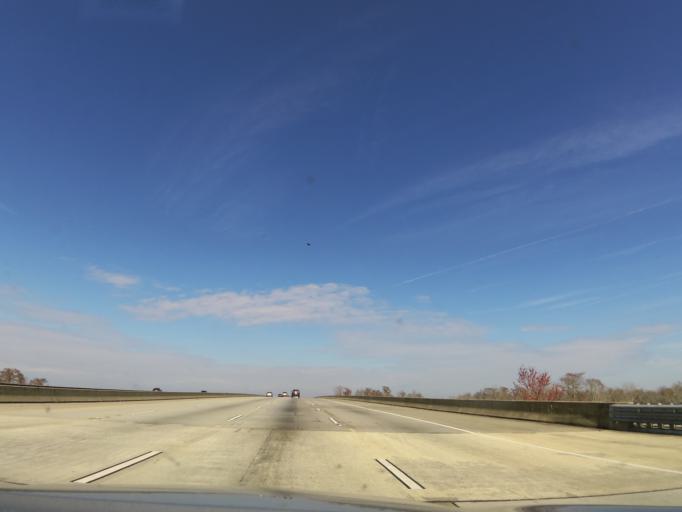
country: US
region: Georgia
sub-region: McIntosh County
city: Darien
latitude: 31.3341
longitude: -81.4681
